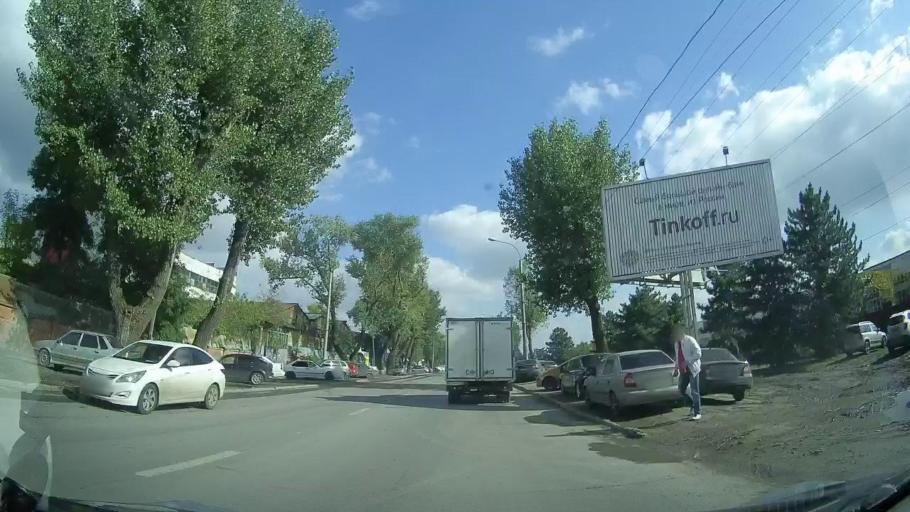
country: RU
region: Rostov
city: Imeni Chkalova
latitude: 47.2671
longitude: 39.7634
